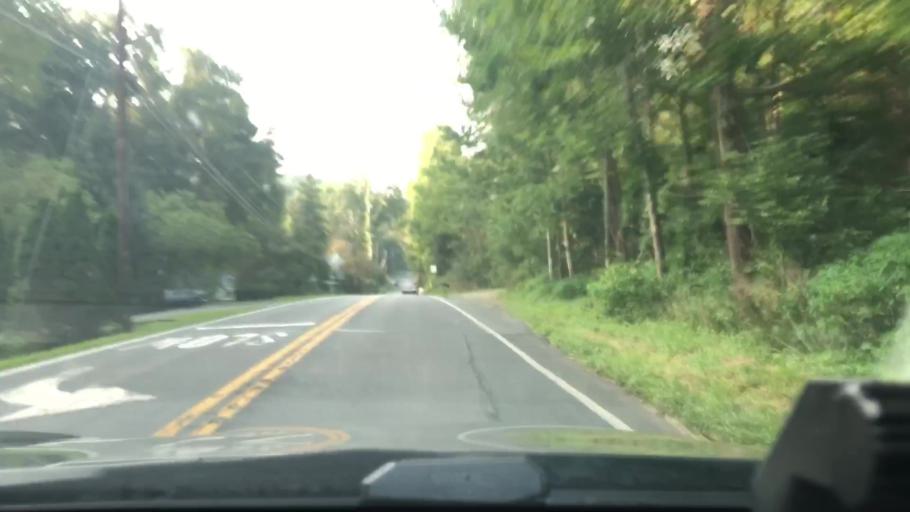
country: US
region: Pennsylvania
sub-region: Berks County
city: Kutztown
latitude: 40.5388
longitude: -75.8001
